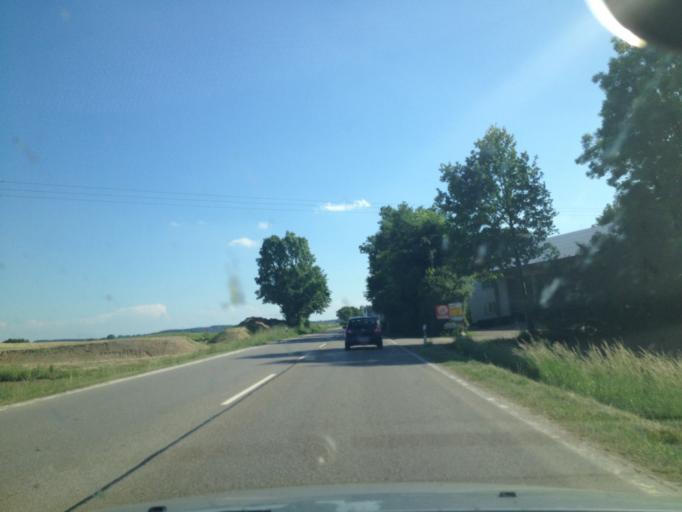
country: DE
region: Bavaria
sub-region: Swabia
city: Obergriesbach
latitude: 48.4094
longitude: 11.0870
